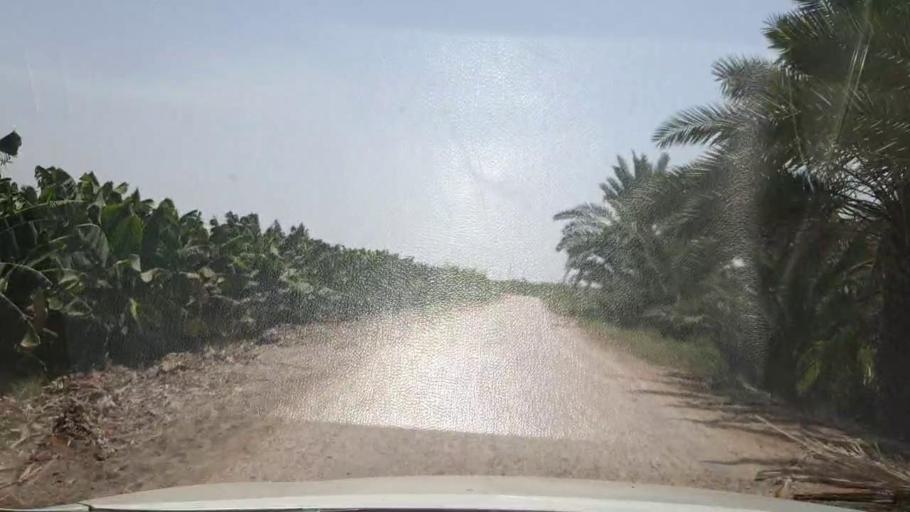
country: PK
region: Sindh
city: Bozdar
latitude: 27.2168
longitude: 68.6576
